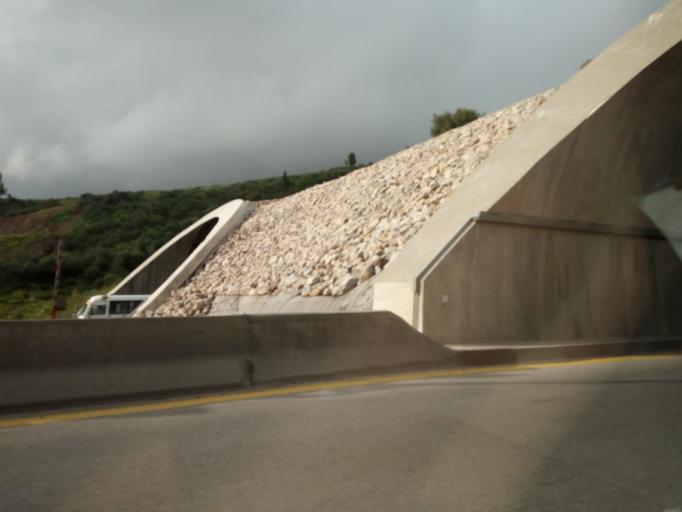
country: DZ
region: Boumerdes
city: Arbatache
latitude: 36.5754
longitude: 3.4103
